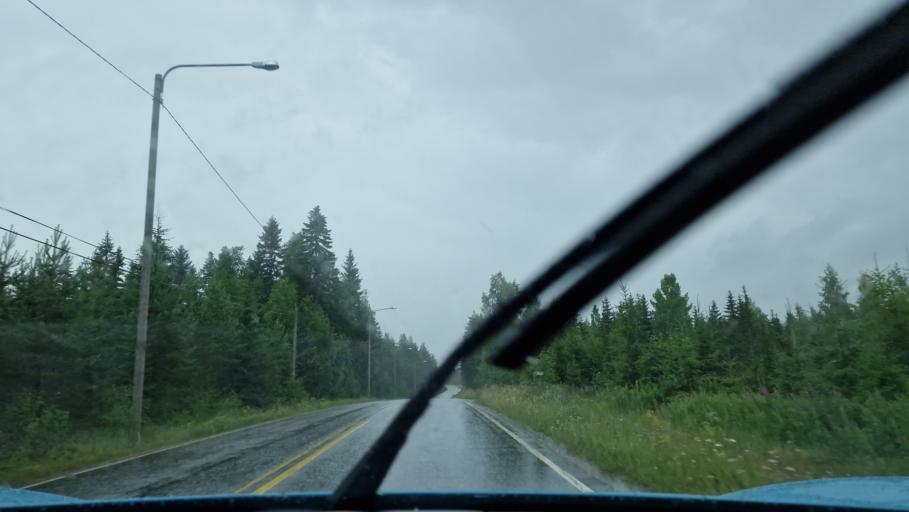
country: FI
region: Southern Ostrobothnia
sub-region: Jaerviseutu
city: Soini
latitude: 62.8372
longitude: 24.3306
